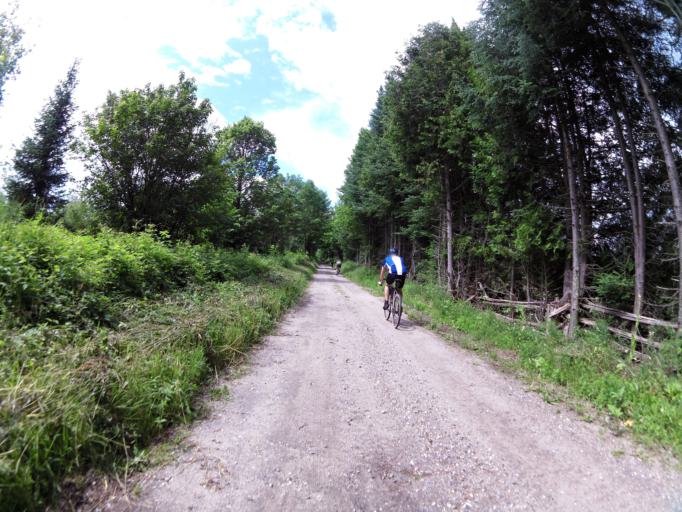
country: CA
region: Ontario
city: Perth
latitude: 45.0260
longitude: -76.5485
